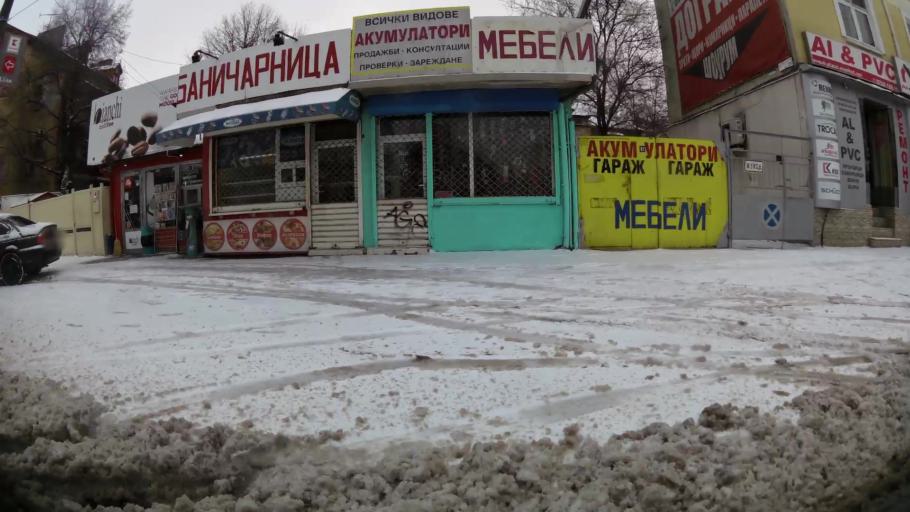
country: BG
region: Sofia-Capital
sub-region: Stolichna Obshtina
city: Sofia
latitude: 42.7052
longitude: 23.3118
